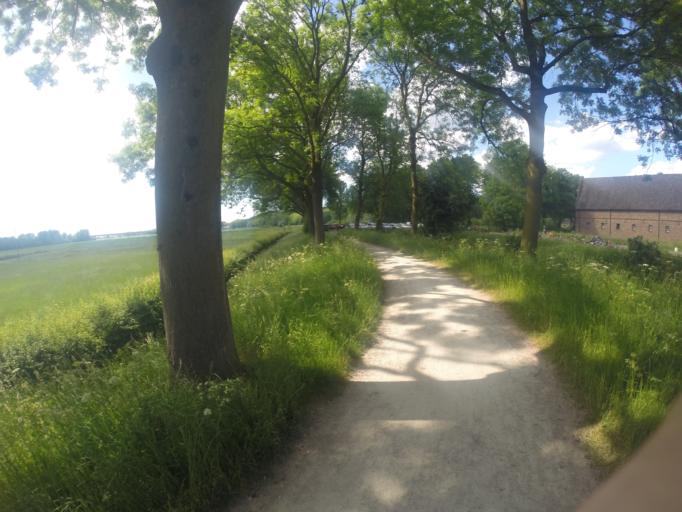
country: NL
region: Gelderland
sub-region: Gemeente Renkum
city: Doorwerth
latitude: 51.9661
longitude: 5.7875
